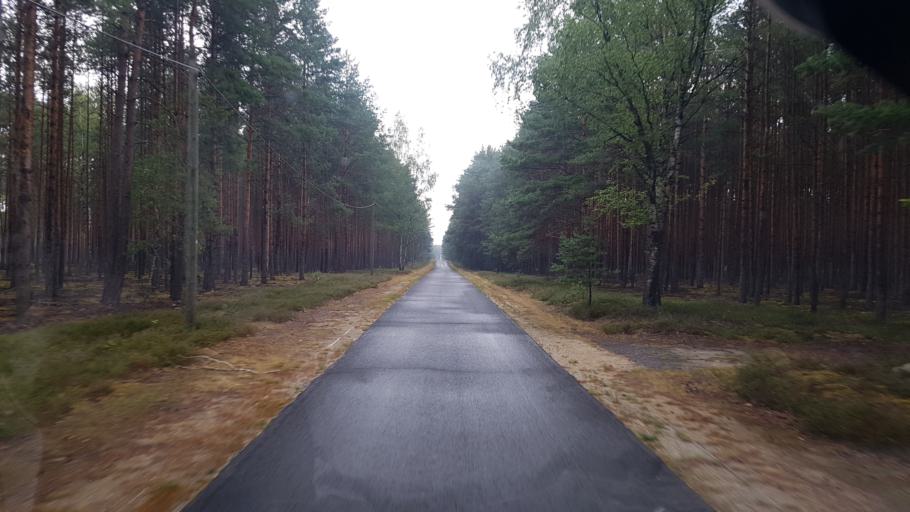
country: DE
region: Brandenburg
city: Finsterwalde
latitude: 51.6508
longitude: 13.7834
